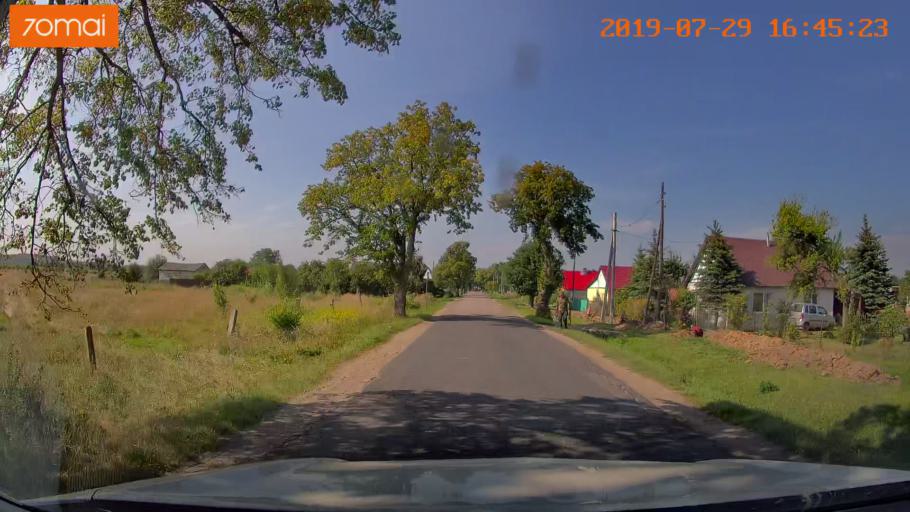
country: RU
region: Kaliningrad
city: Primorsk
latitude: 54.7643
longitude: 20.0809
